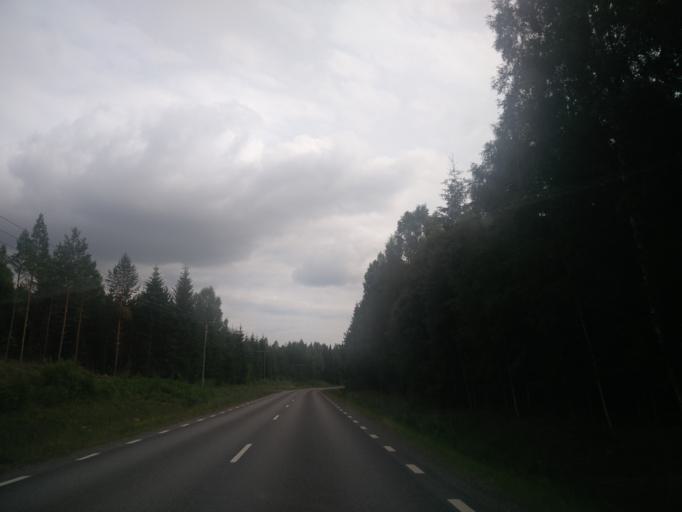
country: SE
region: Vaermland
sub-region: Arvika Kommun
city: Arvika
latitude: 59.7245
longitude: 12.5671
